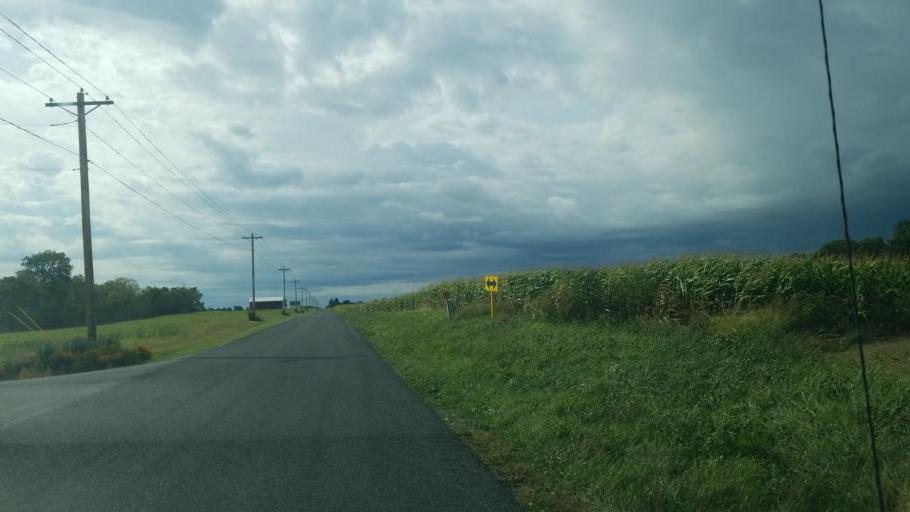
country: US
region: Ohio
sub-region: Hancock County
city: Arlington
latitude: 40.8631
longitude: -83.5755
